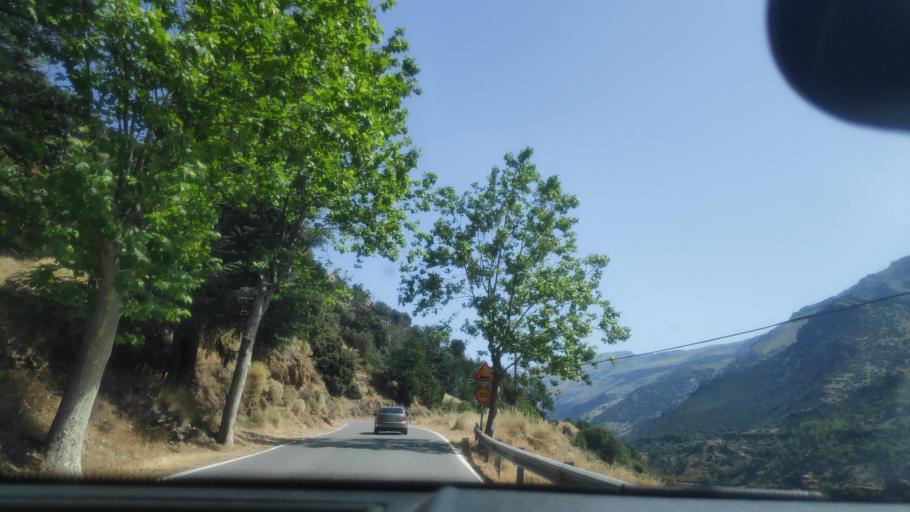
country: ES
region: Andalusia
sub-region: Provincia de Granada
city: Trevelez
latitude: 36.9845
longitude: -3.2732
